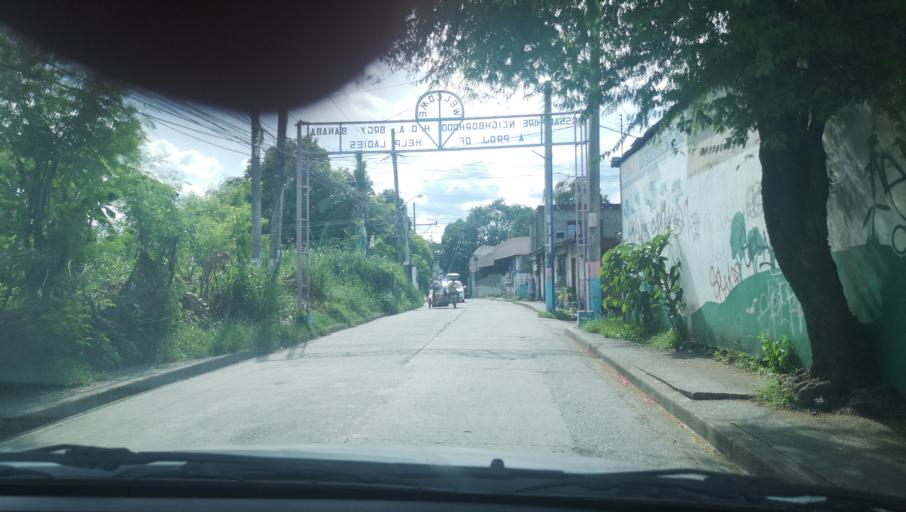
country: PH
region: Calabarzon
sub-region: Province of Rizal
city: San Mateo
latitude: 14.6744
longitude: 121.1118
